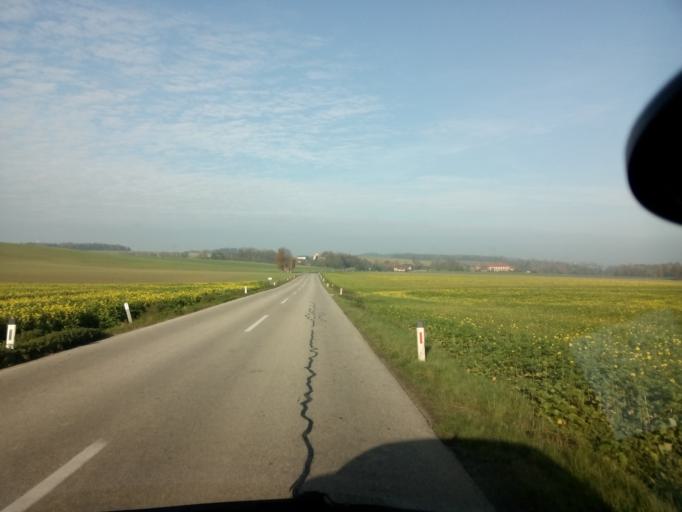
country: AT
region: Upper Austria
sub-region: Politischer Bezirk Linz-Land
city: Ansfelden
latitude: 48.1758
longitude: 14.3041
